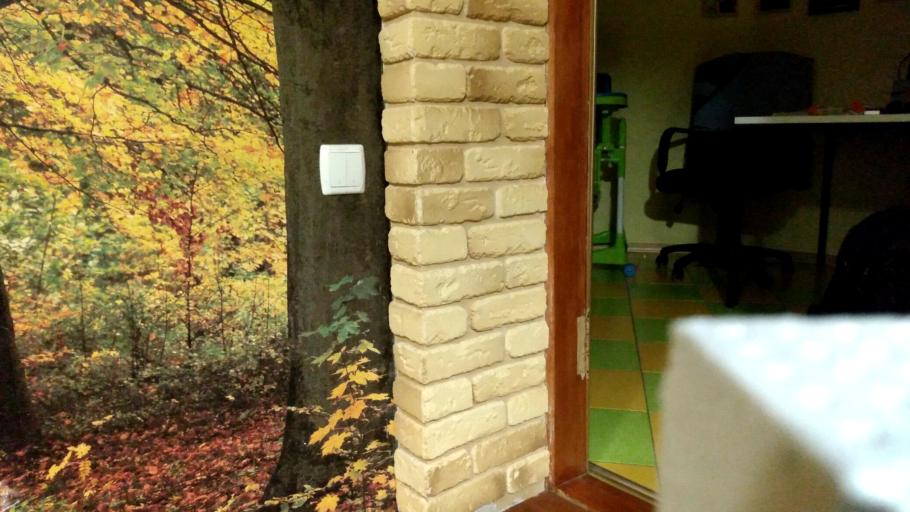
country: RU
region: Arkhangelskaya
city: Kargopol'
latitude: 61.5387
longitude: 37.7662
